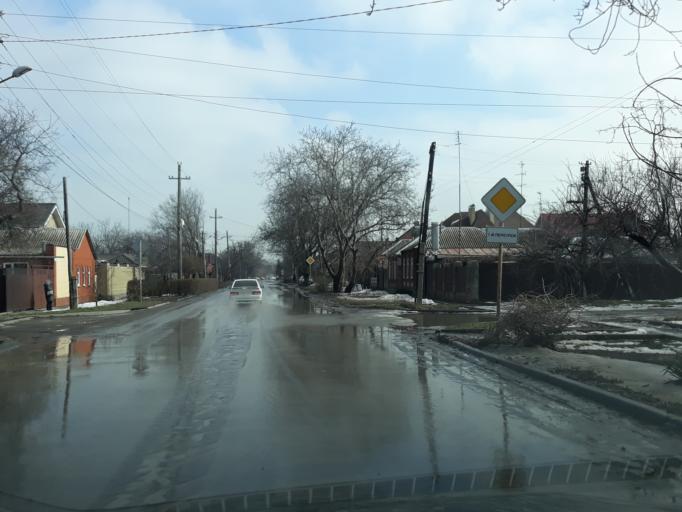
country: RU
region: Rostov
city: Taganrog
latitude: 47.2145
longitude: 38.9023
